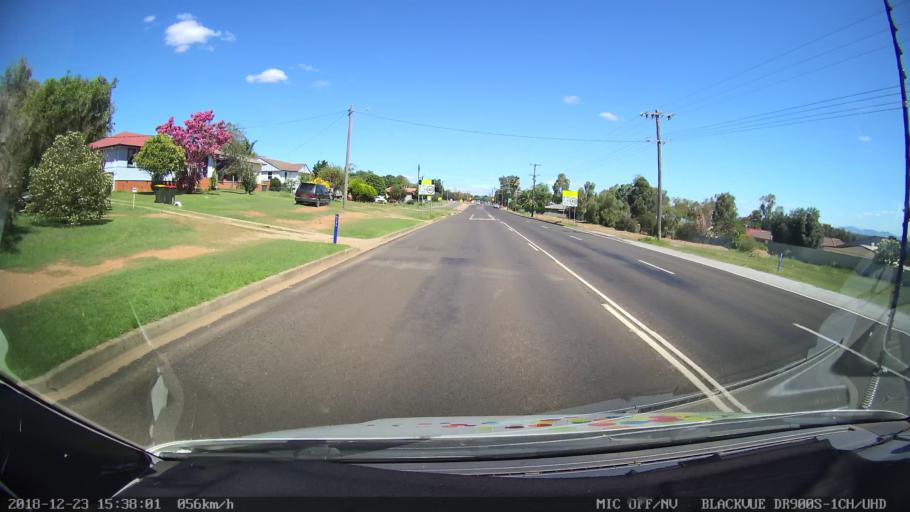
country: AU
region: New South Wales
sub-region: Tamworth Municipality
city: Tamworth
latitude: -31.0562
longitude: 150.8938
